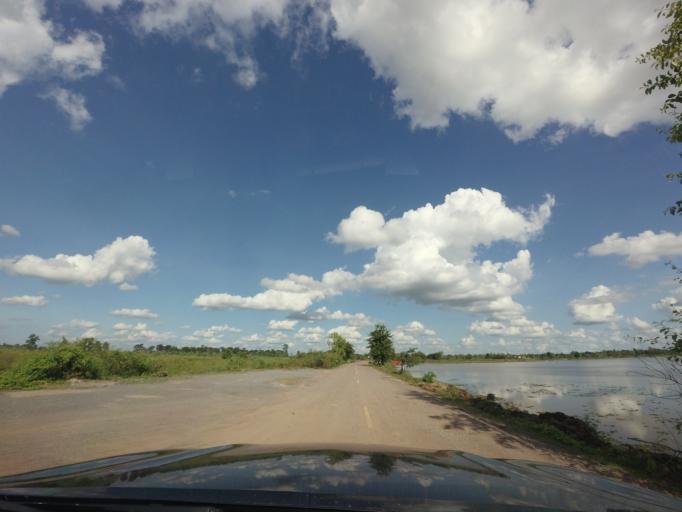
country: TH
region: Changwat Udon Thani
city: Ban Dung
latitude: 17.7504
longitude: 103.3601
